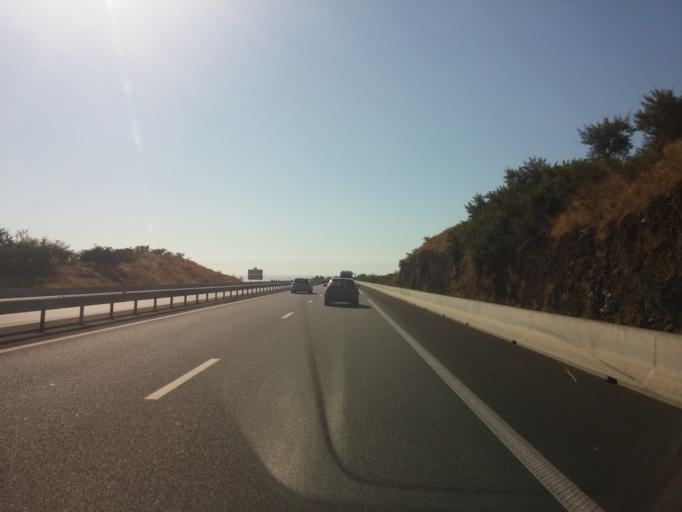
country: RE
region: Reunion
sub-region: Reunion
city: Trois-Bassins
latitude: -21.0729
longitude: 55.2509
